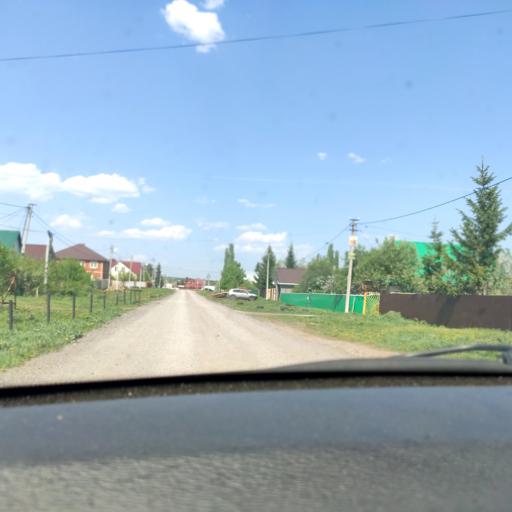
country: RU
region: Bashkortostan
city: Mikhaylovka
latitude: 54.8951
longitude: 55.8786
